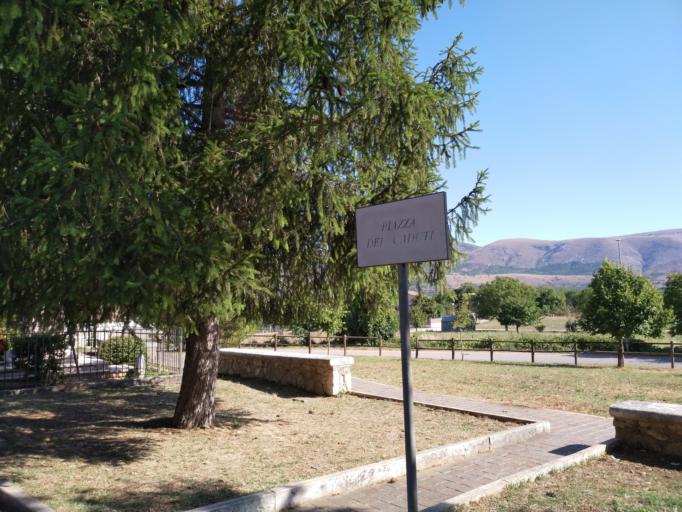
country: IT
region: Abruzzo
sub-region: Provincia dell' Aquila
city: Secinaro
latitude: 42.1802
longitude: 13.6690
